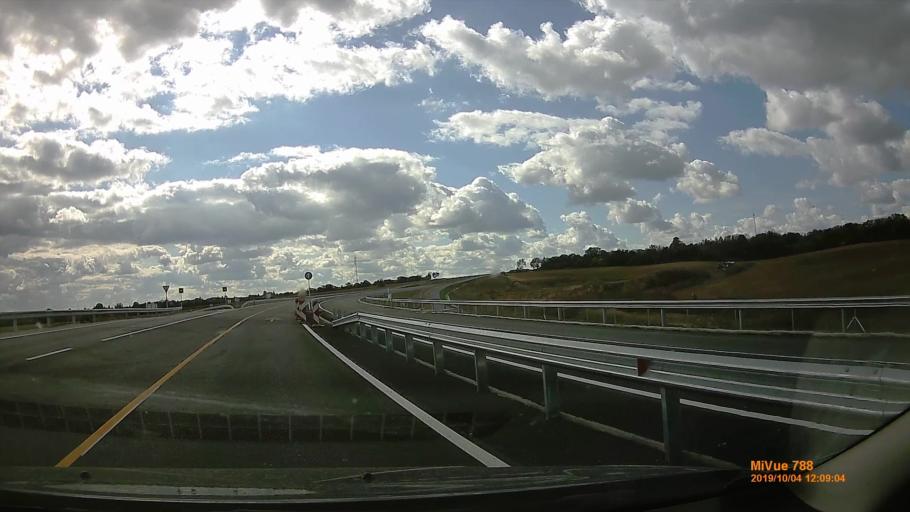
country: HU
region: Somogy
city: Kaposvar
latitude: 46.5213
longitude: 17.8182
